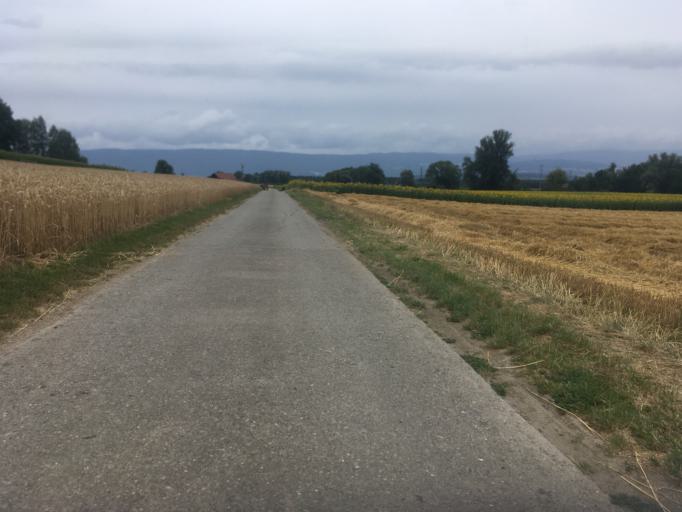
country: CH
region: Fribourg
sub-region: See District
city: Bas-Vully
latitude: 46.9664
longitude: 7.1097
